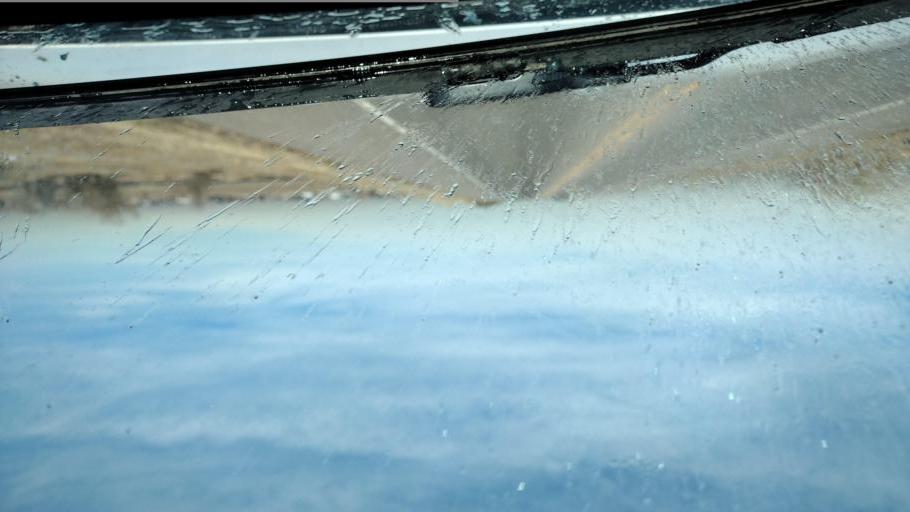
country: US
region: Colorado
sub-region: Adams County
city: Brighton
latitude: 39.9263
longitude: -104.8184
